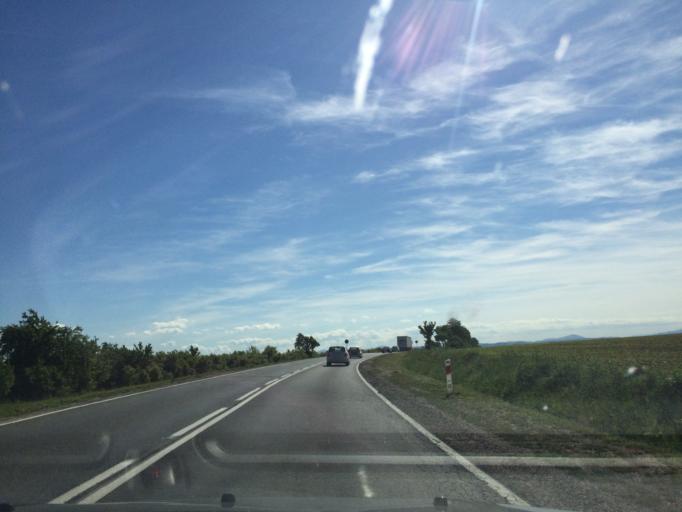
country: PL
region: Lower Silesian Voivodeship
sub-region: Powiat swidnicki
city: Zarow
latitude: 50.8910
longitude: 16.6092
